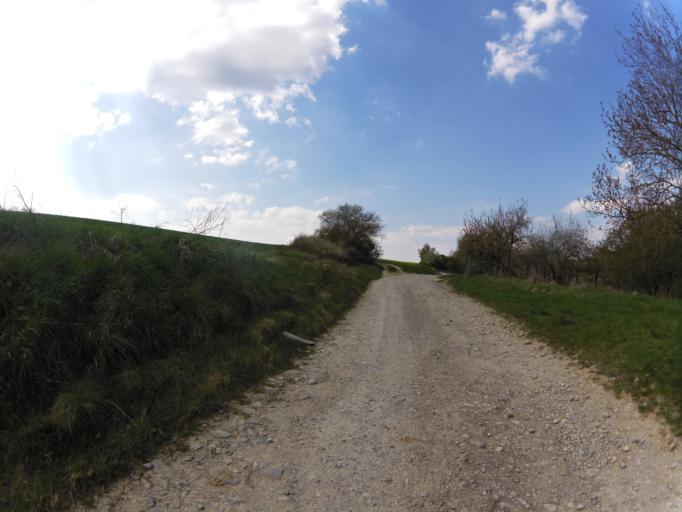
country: DE
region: Bavaria
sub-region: Regierungsbezirk Unterfranken
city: Sommerhausen
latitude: 49.6847
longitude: 10.0177
